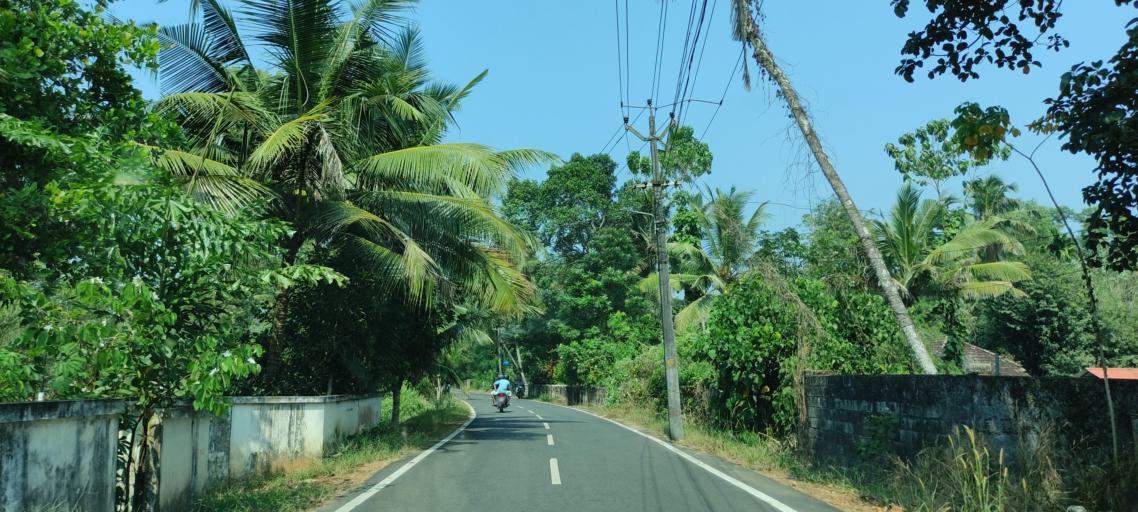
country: IN
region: Kerala
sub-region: Alappuzha
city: Shertallai
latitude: 9.5975
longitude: 76.3117
